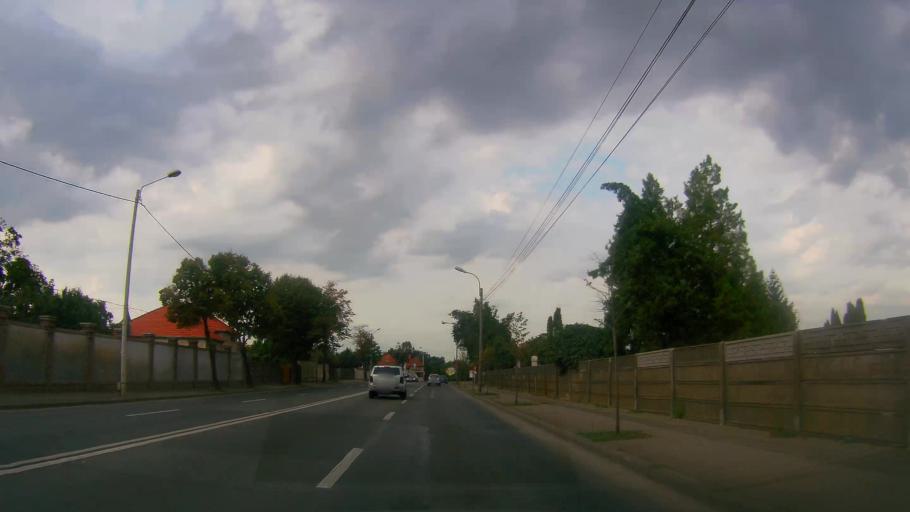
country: RO
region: Satu Mare
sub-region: Municipiul Satu Mare
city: Satu Mare
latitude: 47.7909
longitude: 22.8913
